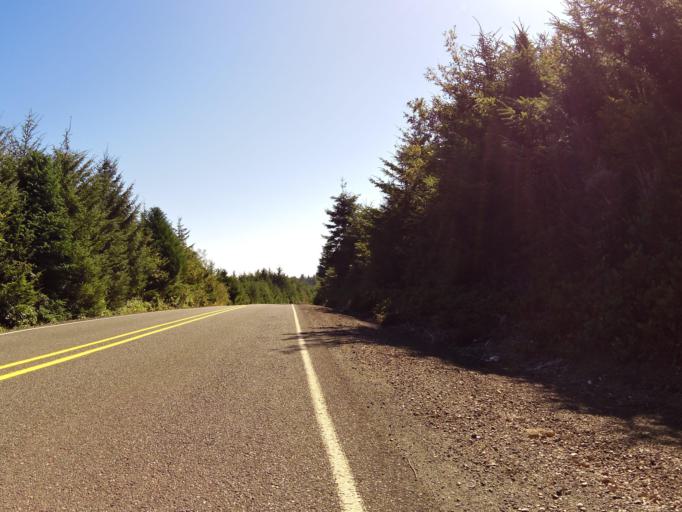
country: US
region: Oregon
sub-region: Coos County
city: Barview
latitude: 43.2702
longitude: -124.3475
